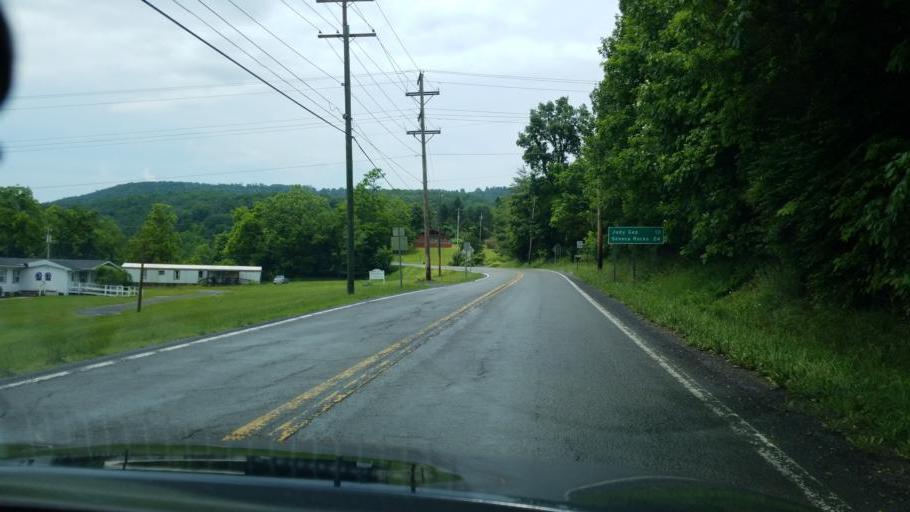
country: US
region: West Virginia
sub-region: Pendleton County
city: Franklin
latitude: 38.6560
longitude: -79.3339
